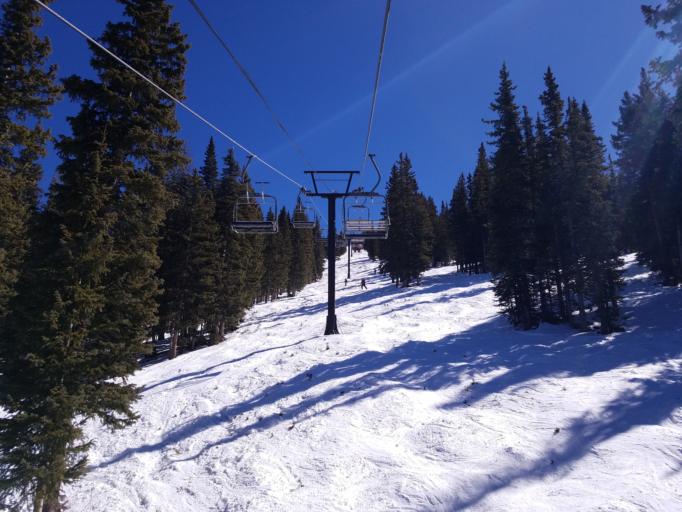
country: US
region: New Mexico
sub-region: Santa Fe County
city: Santa Fe
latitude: 35.7899
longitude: -105.7900
